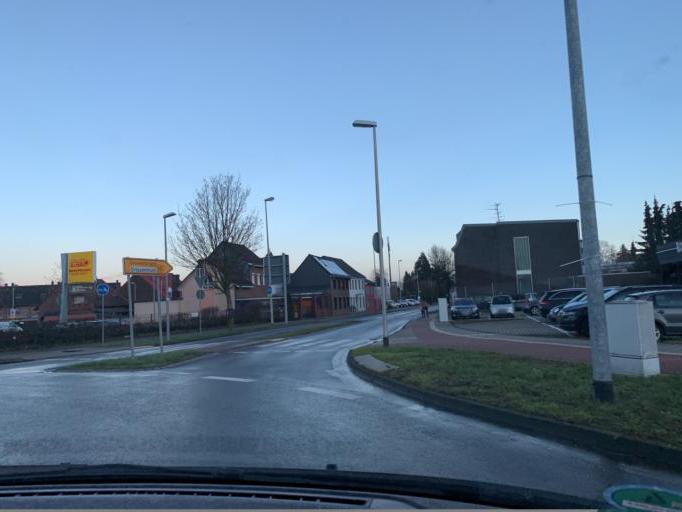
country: DE
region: North Rhine-Westphalia
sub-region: Regierungsbezirk Dusseldorf
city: Juchen
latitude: 51.1036
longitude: 6.4969
